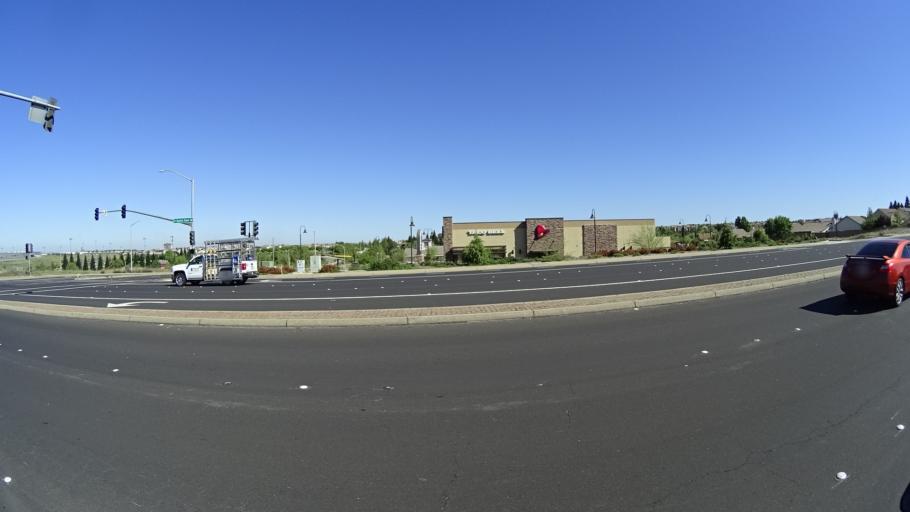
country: US
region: California
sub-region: Placer County
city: Rocklin
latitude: 38.8184
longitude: -121.2805
